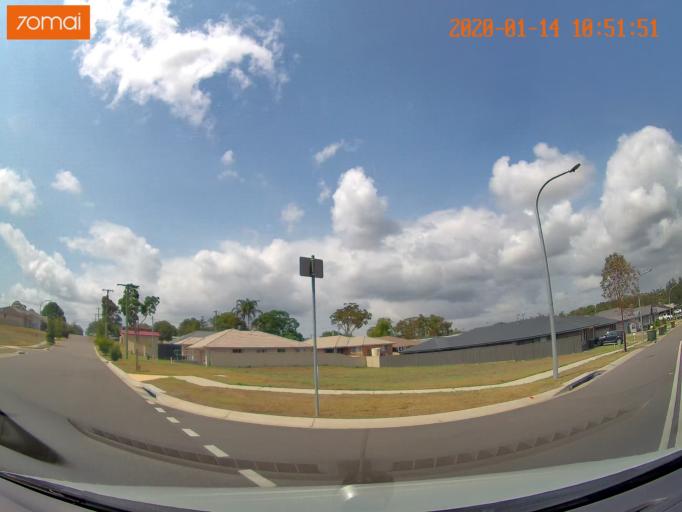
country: AU
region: New South Wales
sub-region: Lake Macquarie Shire
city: Dora Creek
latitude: -33.0991
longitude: 151.4843
